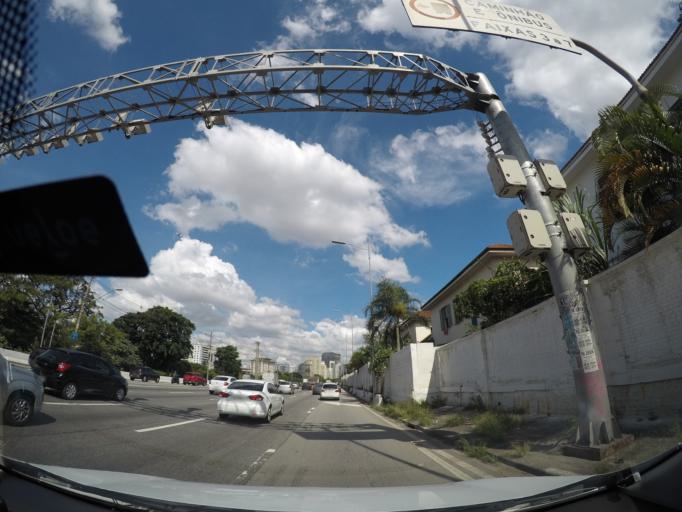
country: BR
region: Sao Paulo
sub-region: Sao Paulo
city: Sao Paulo
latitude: -23.5751
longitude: -46.6994
